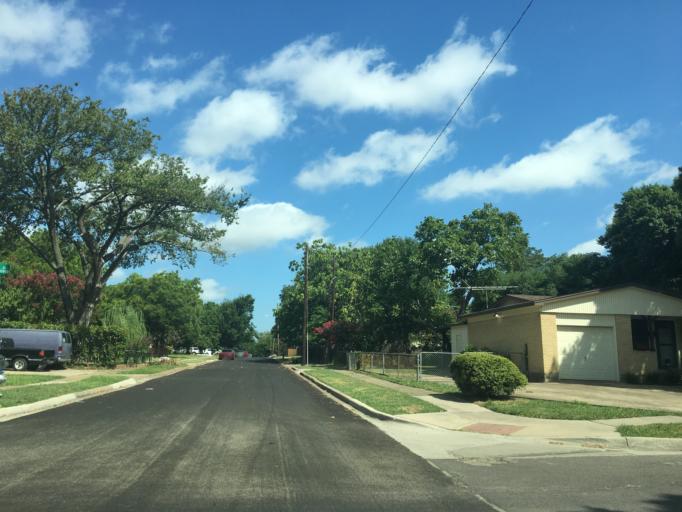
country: US
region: Texas
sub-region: Dallas County
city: Garland
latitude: 32.8407
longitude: -96.6580
